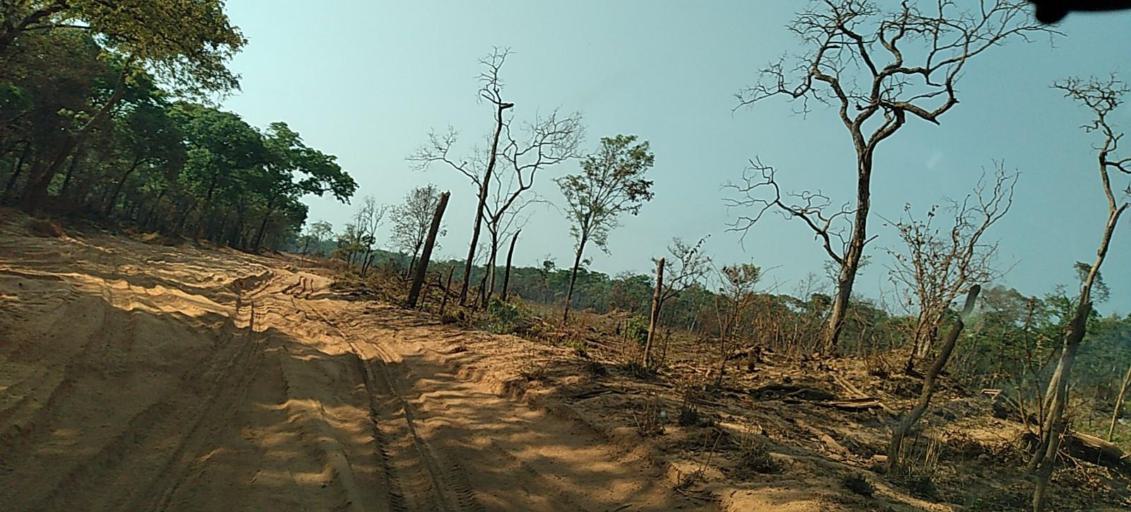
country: ZM
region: North-Western
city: Kasempa
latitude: -13.6350
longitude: 25.9919
